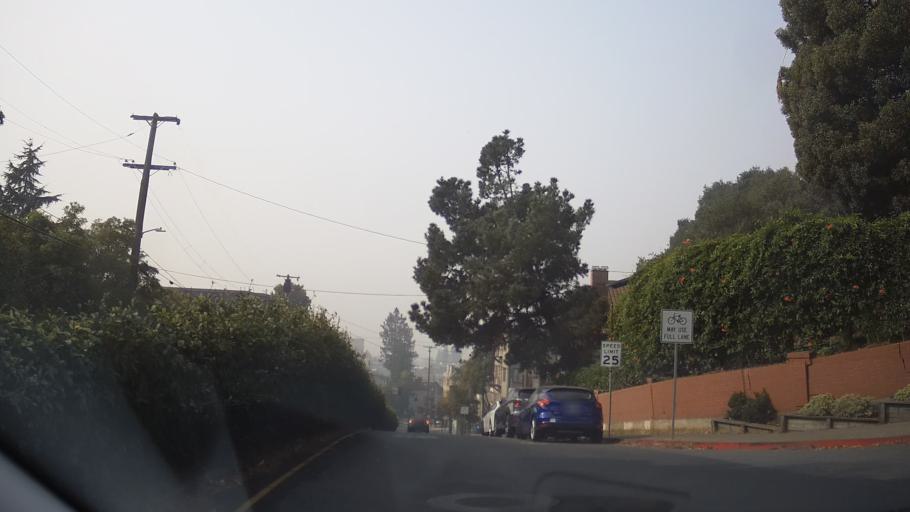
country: US
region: California
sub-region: Alameda County
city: Berkeley
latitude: 37.8748
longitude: -122.2622
